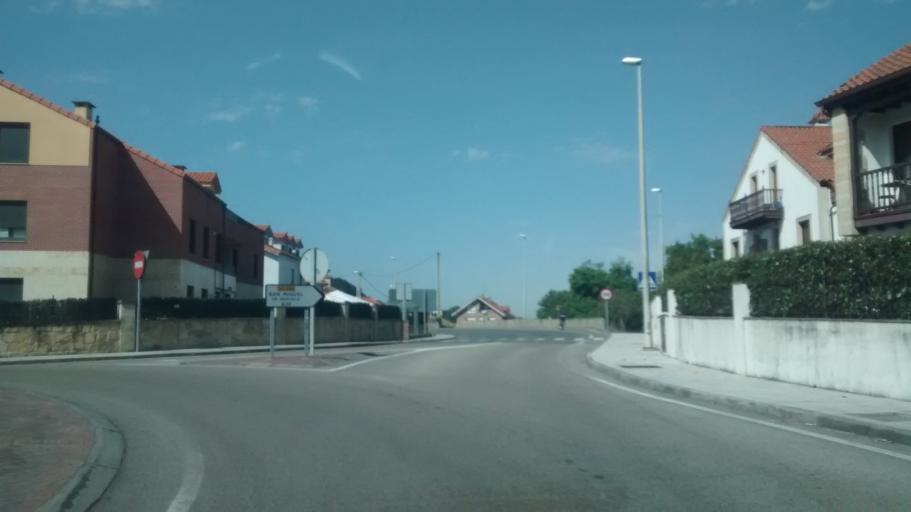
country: ES
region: Cantabria
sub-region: Provincia de Cantabria
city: San Miguel de Meruelo
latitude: 43.4459
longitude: -3.5656
